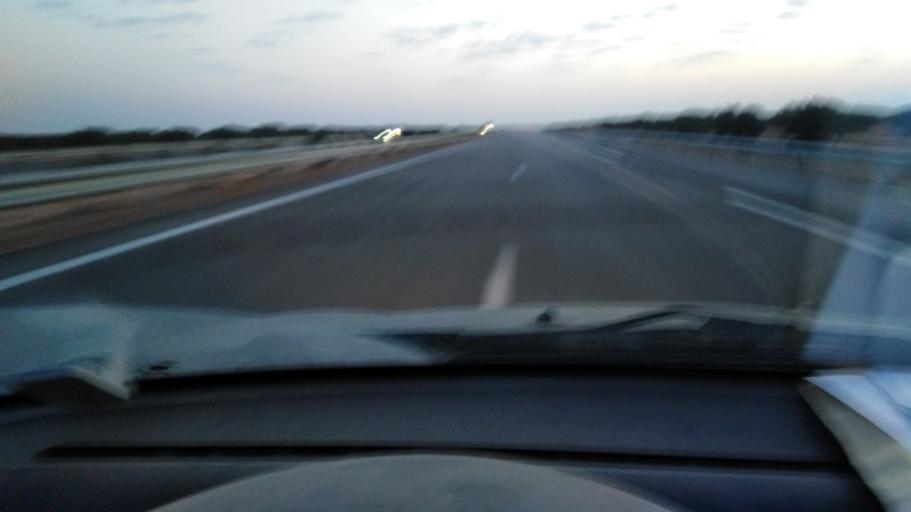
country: TN
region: Safaqis
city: Bi'r `Ali Bin Khalifah
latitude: 34.5391
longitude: 10.2968
